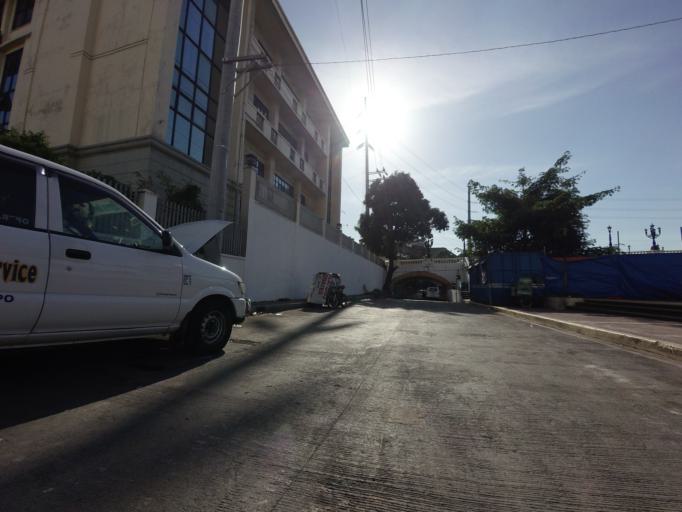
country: PH
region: Metro Manila
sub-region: City of Manila
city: Quiapo
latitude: 14.5955
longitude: 120.9780
